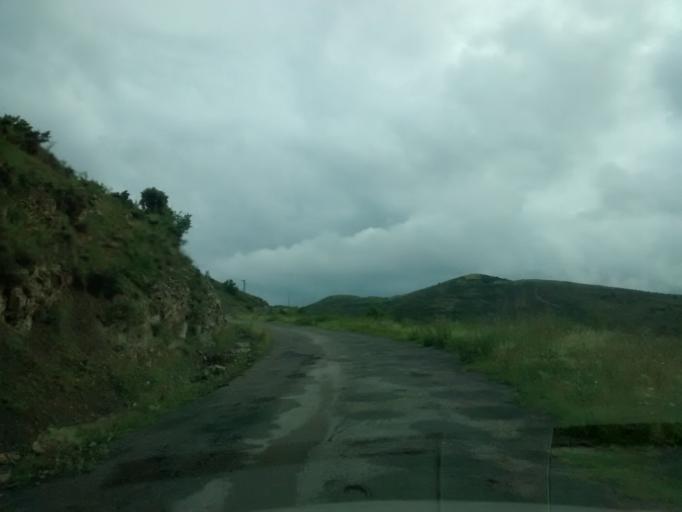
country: ES
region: La Rioja
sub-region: Provincia de La Rioja
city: San Roman de Cameros
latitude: 42.2196
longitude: -2.4616
